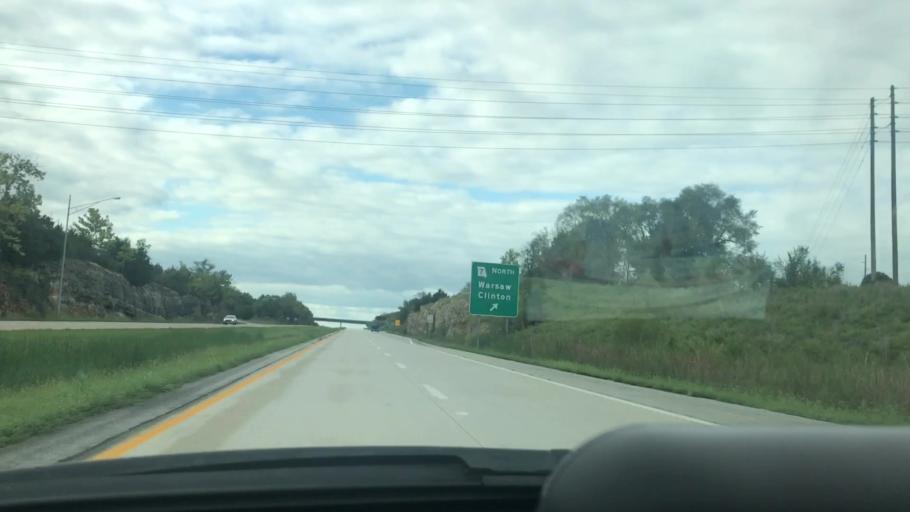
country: US
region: Missouri
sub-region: Benton County
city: Warsaw
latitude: 38.2481
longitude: -93.3611
